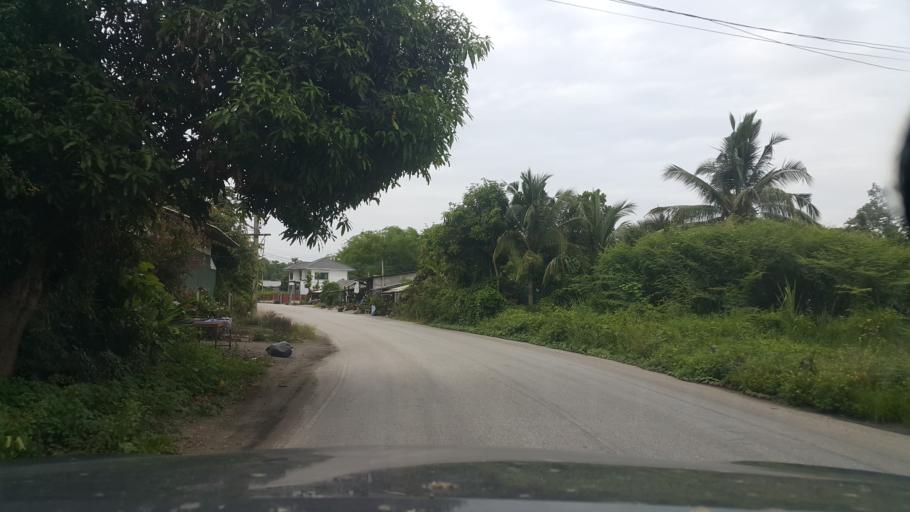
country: TH
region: Chiang Mai
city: San Pa Tong
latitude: 18.6597
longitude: 98.8351
